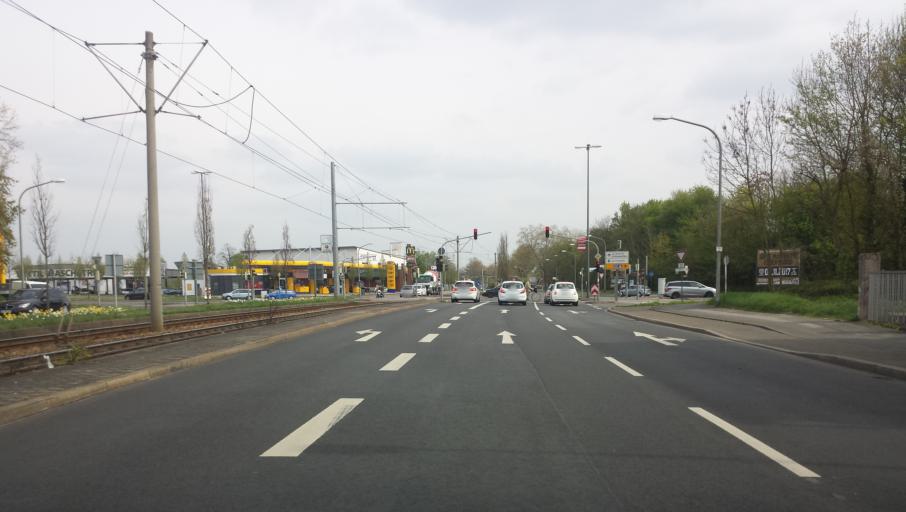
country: DE
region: Rheinland-Pfalz
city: Gartenstadt
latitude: 49.4891
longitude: 8.3822
